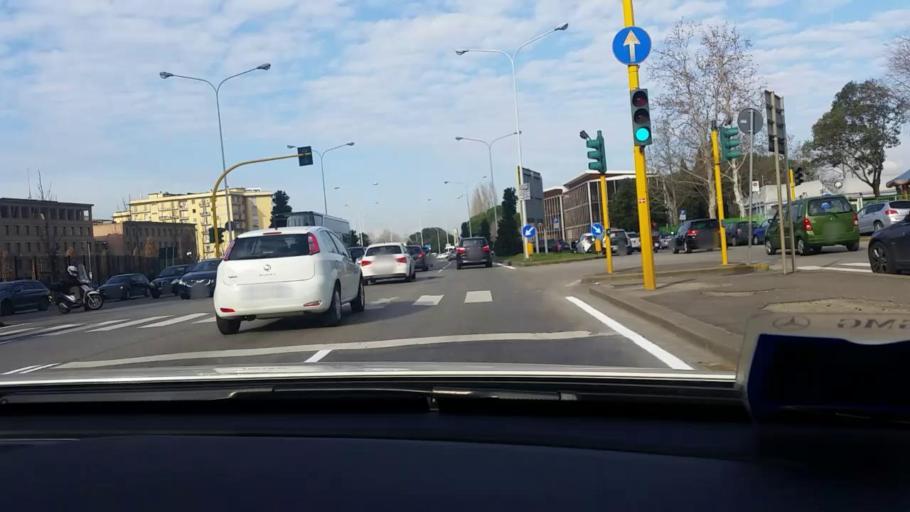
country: IT
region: Tuscany
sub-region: Province of Florence
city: Florence
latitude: 43.7966
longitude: 11.2257
